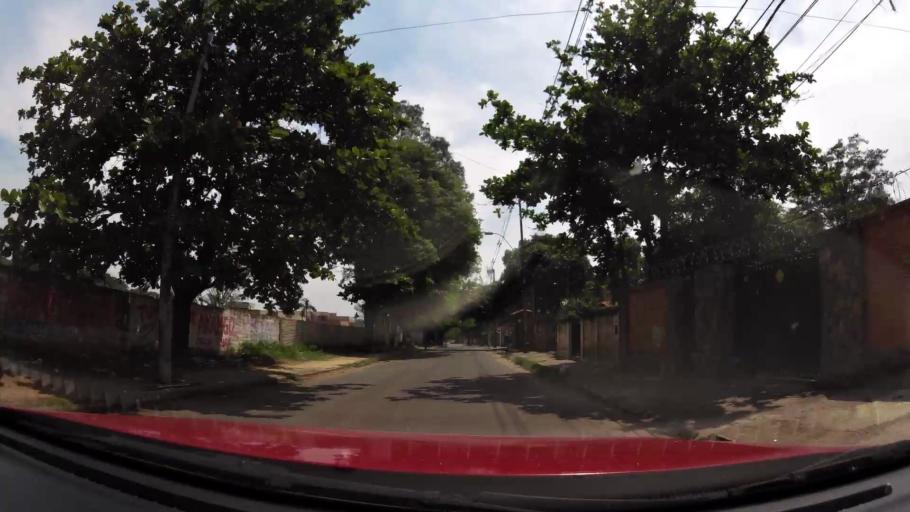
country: PY
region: Asuncion
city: Asuncion
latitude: -25.2822
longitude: -57.5903
